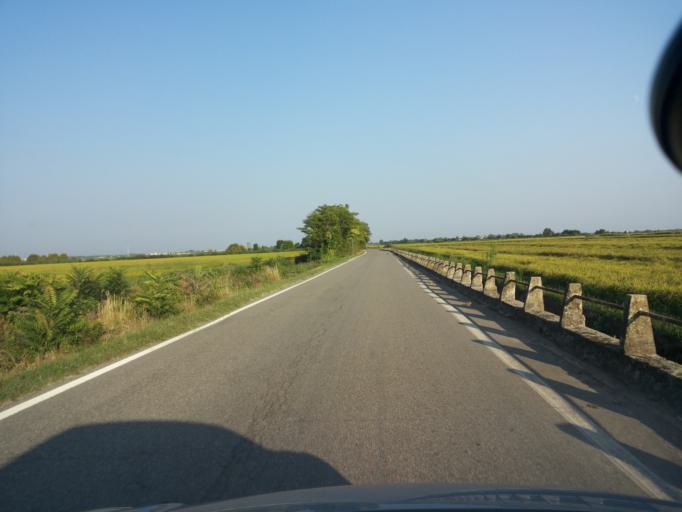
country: IT
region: Piedmont
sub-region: Provincia di Vercelli
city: Sali Vercellese
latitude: 45.3067
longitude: 8.3331
